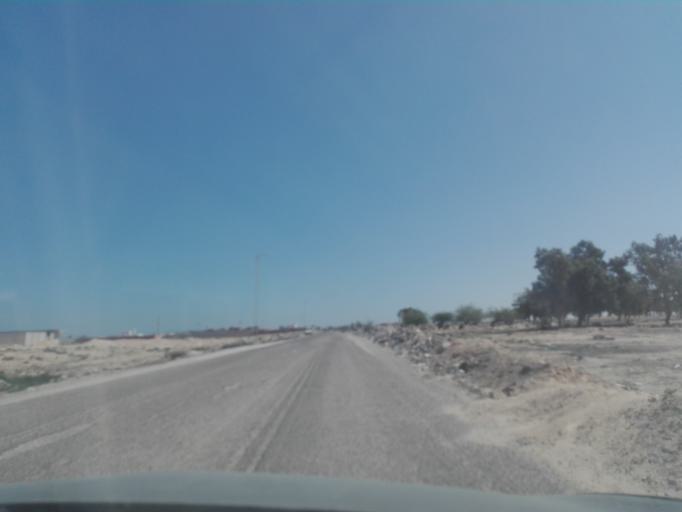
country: TN
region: Qabis
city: Gabes
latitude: 33.8711
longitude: 10.0403
